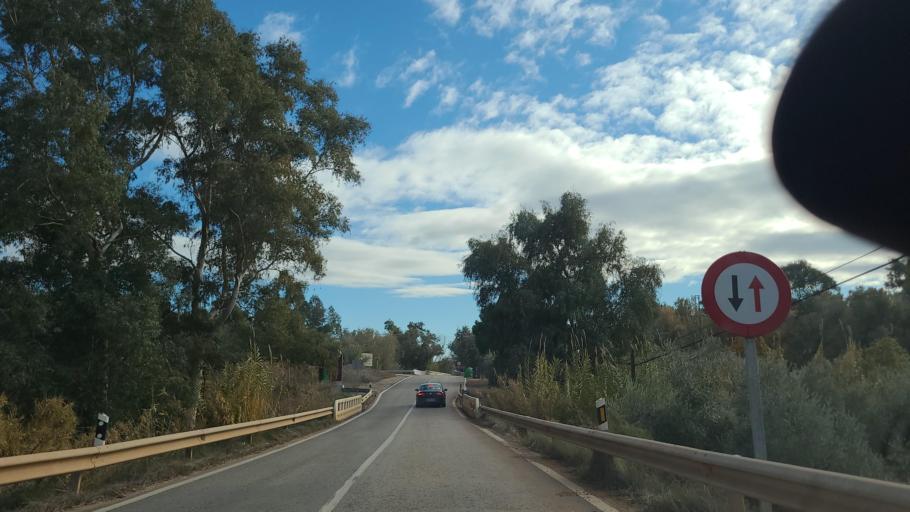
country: ES
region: Andalusia
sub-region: Provincia de Jaen
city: Villanueva de la Reina
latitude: 38.0278
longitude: -3.9171
